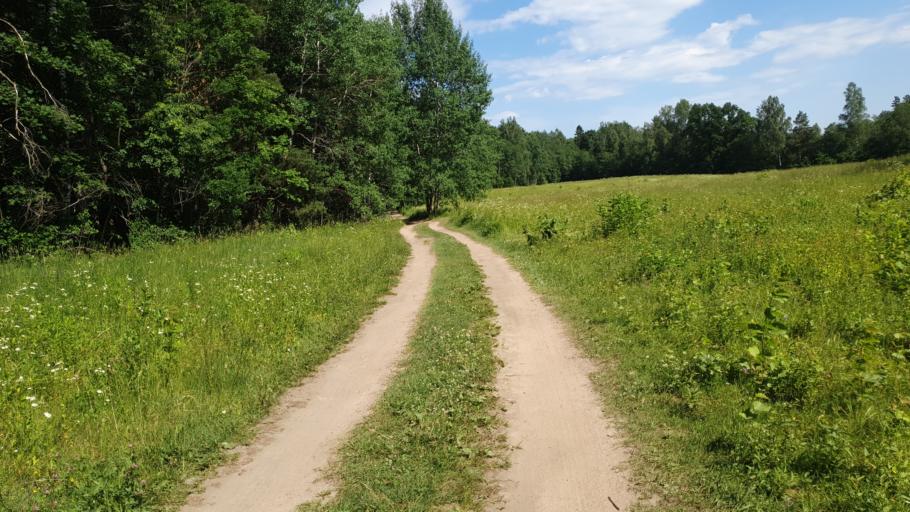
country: LT
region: Vilnius County
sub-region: Vilnius
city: Fabijoniskes
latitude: 54.7881
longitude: 25.3162
